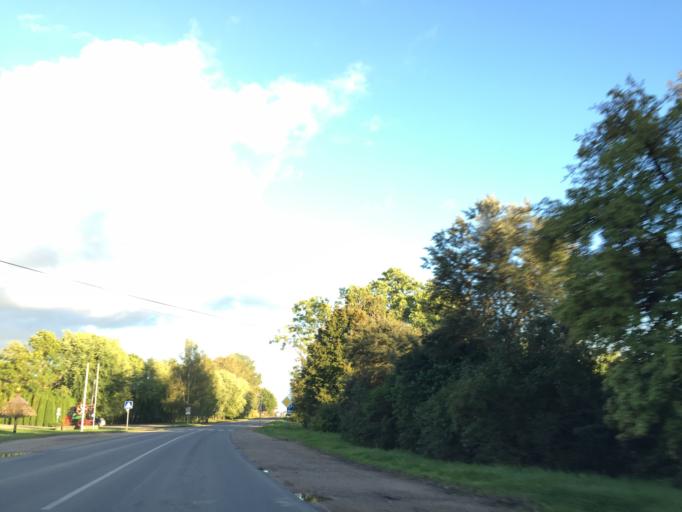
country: LV
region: Saldus Rajons
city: Saldus
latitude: 56.6931
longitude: 22.4456
